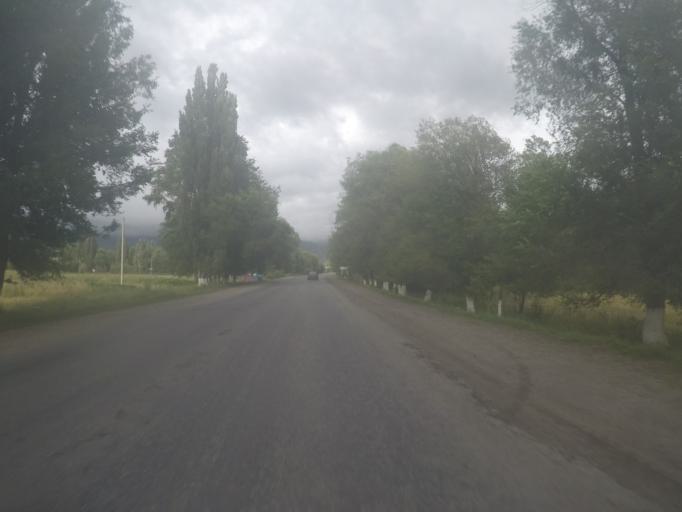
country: KG
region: Ysyk-Koel
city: Tyup
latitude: 42.7765
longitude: 78.2049
